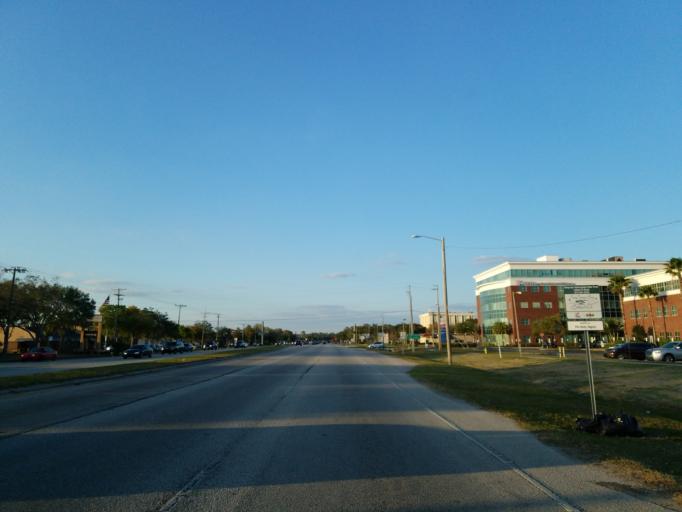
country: US
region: Florida
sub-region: Hillsborough County
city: University
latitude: 28.0701
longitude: -82.4259
